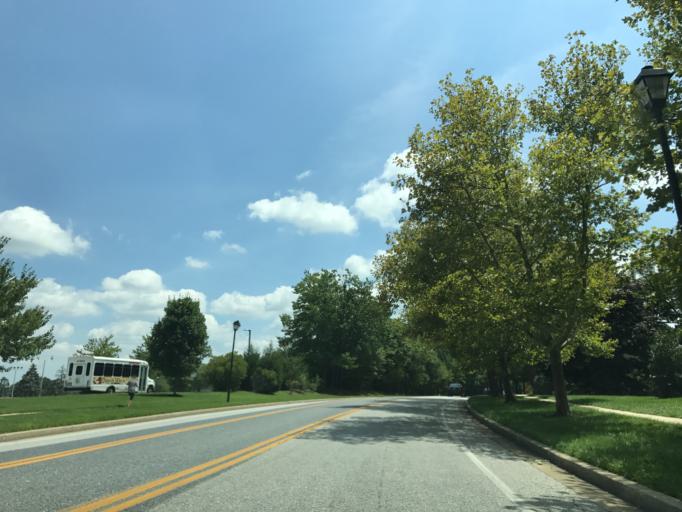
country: US
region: Maryland
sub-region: Howard County
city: Riverside
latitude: 39.2106
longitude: -76.8796
